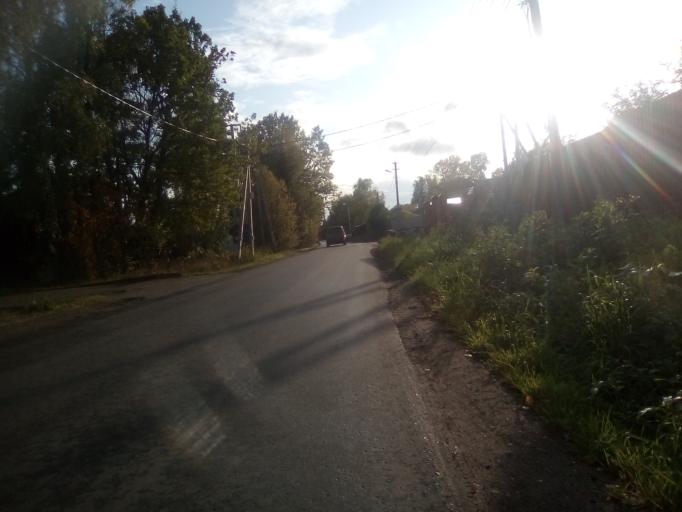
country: RU
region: Moskovskaya
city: Krasnoznamensk
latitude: 55.5697
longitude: 37.0162
